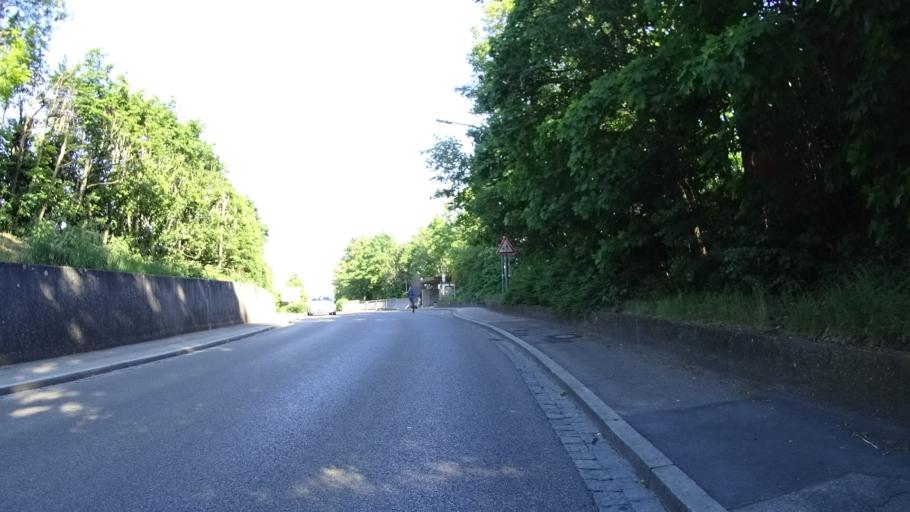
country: DE
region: Bavaria
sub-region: Regierungsbezirk Mittelfranken
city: Feuchtwangen
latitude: 49.1645
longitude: 10.3401
